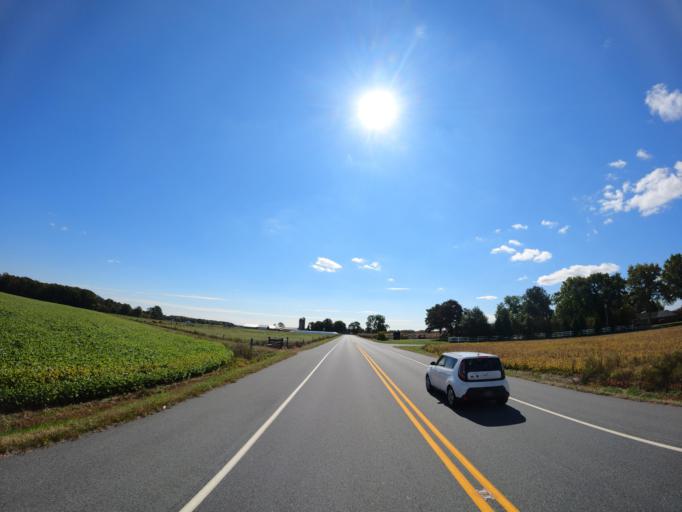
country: US
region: Delaware
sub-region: Sussex County
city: Bridgeville
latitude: 38.8135
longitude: -75.6166
